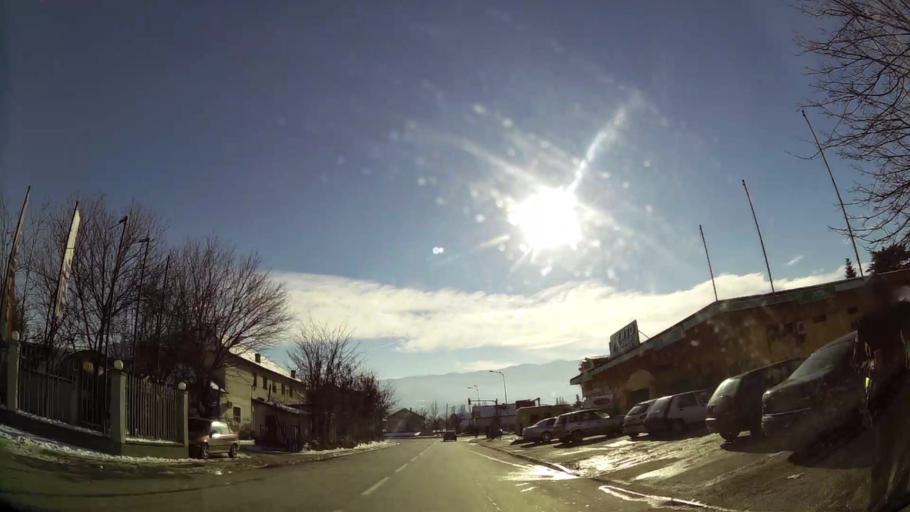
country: MK
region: Saraj
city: Saraj
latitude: 42.0079
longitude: 21.3399
